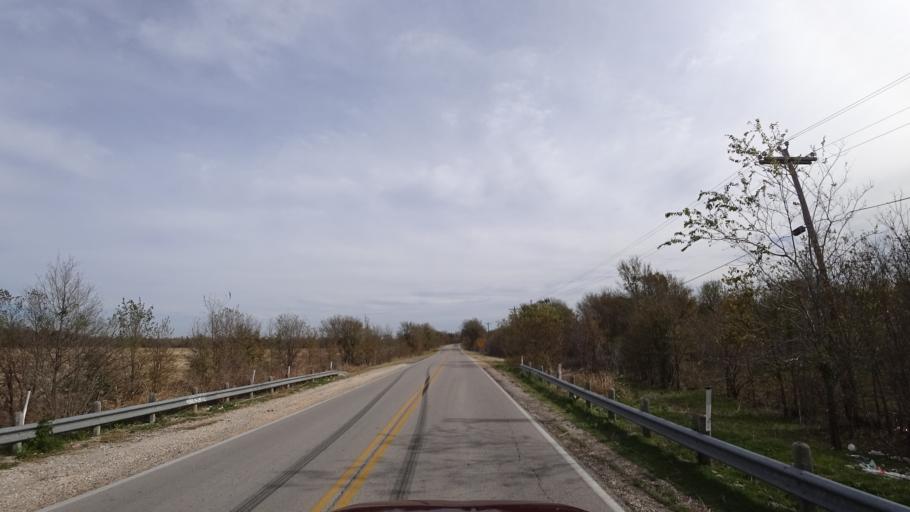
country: US
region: Texas
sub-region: Travis County
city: Garfield
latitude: 30.1324
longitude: -97.6087
